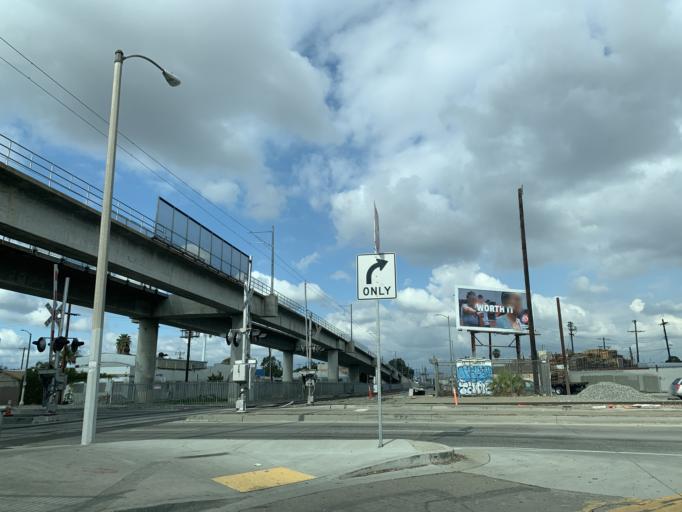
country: US
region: California
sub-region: Los Angeles County
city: Huntington Park
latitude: 33.9891
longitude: -118.2432
